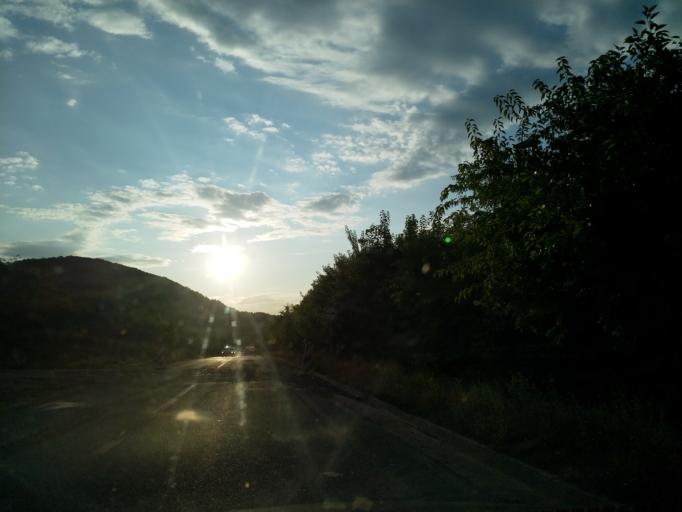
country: RS
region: Central Serbia
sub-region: Rasinski Okrug
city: Trstenik
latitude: 43.6131
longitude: 20.9922
